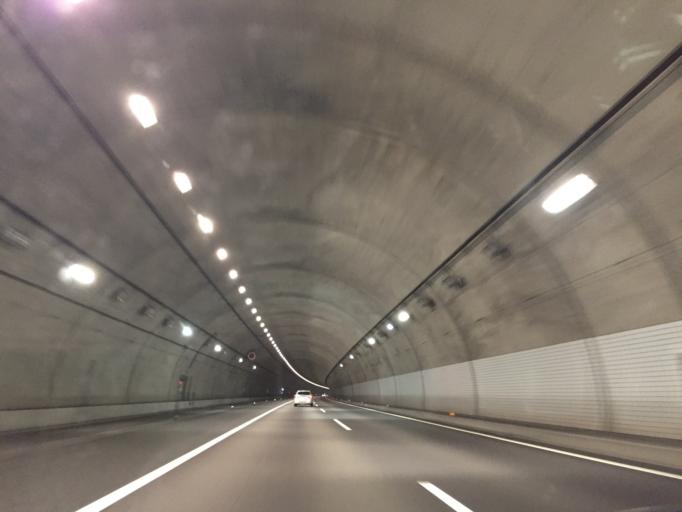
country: JP
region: Shizuoka
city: Shizuoka-shi
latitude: 35.0991
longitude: 138.4797
